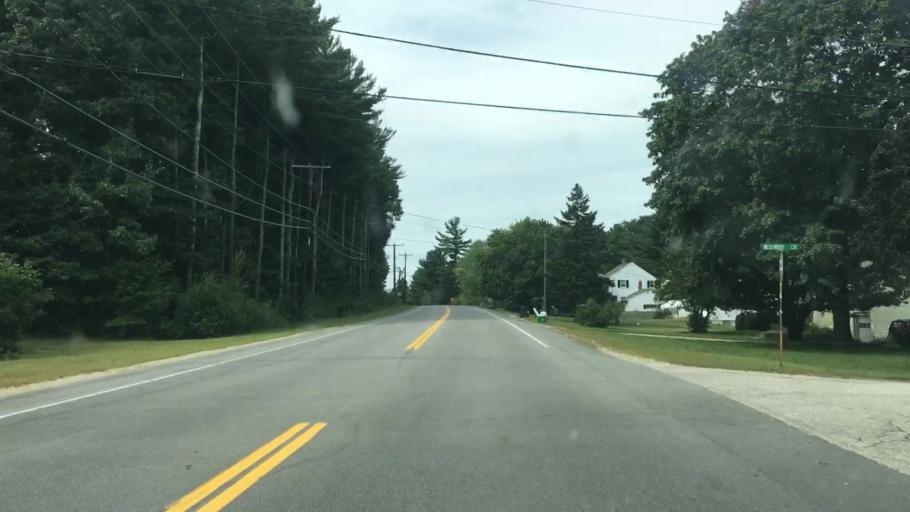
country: US
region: New Hampshire
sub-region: Strafford County
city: Madbury
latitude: 43.1919
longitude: -70.9277
